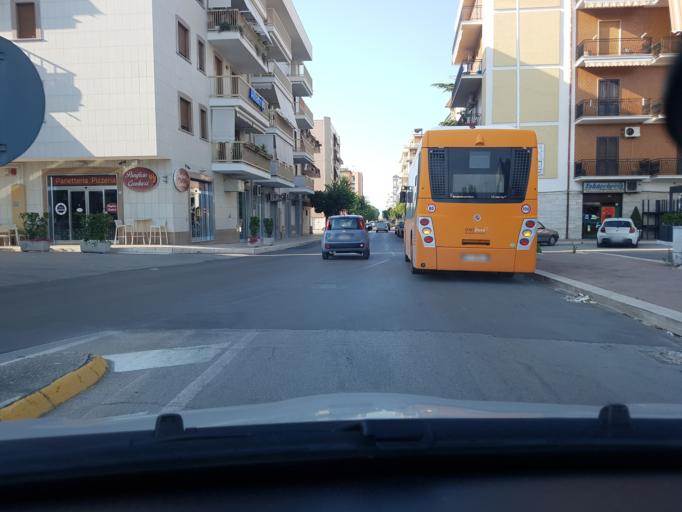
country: IT
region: Apulia
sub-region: Provincia di Foggia
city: Cerignola
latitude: 41.2606
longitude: 15.9075
